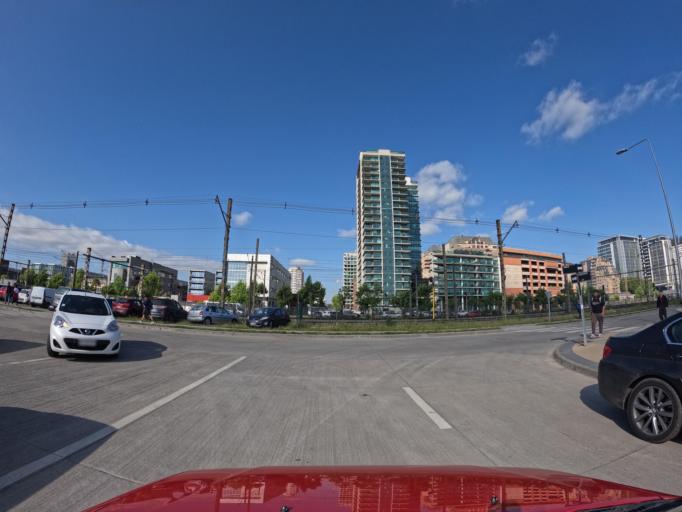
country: CL
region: Biobio
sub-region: Provincia de Concepcion
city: Concepcion
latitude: -36.8320
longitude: -73.0606
